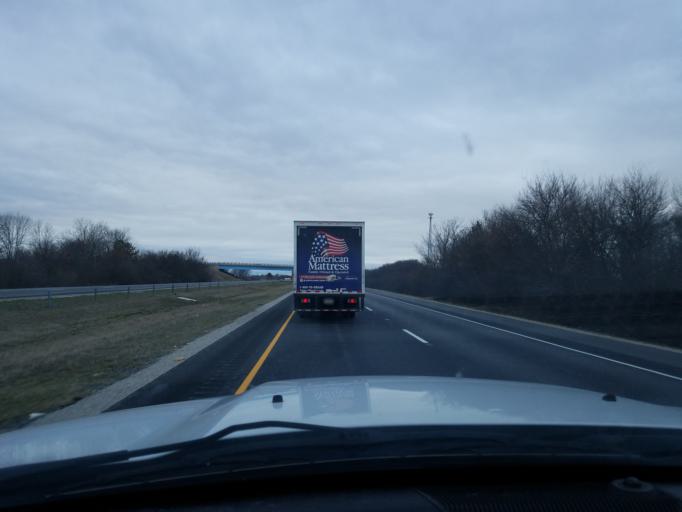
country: US
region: Indiana
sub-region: Boone County
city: Thorntown
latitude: 40.1951
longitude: -86.5714
